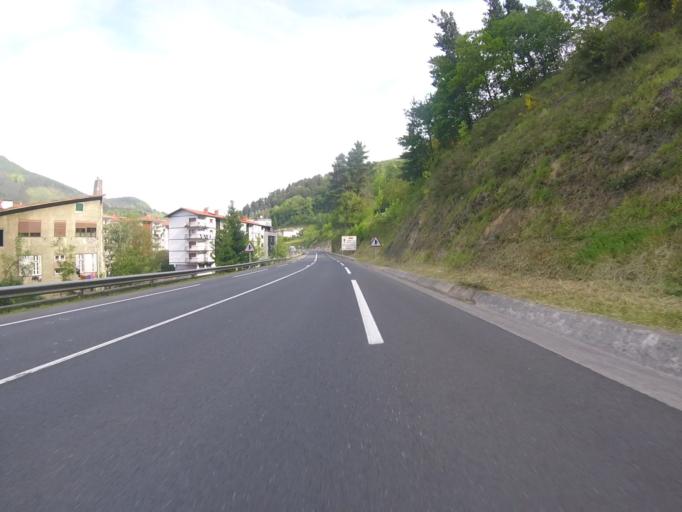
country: ES
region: Basque Country
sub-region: Provincia de Guipuzcoa
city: Zumarraga
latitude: 43.0934
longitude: -2.3115
